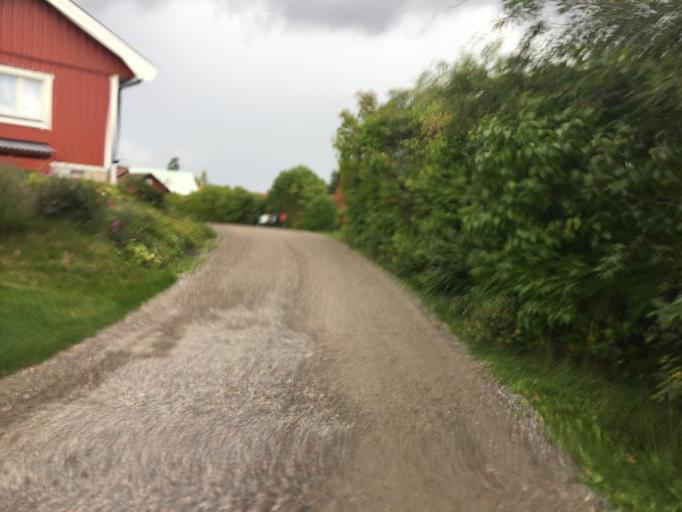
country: SE
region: Soedermanland
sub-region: Eskilstuna Kommun
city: Arla
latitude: 59.4528
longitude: 16.6660
